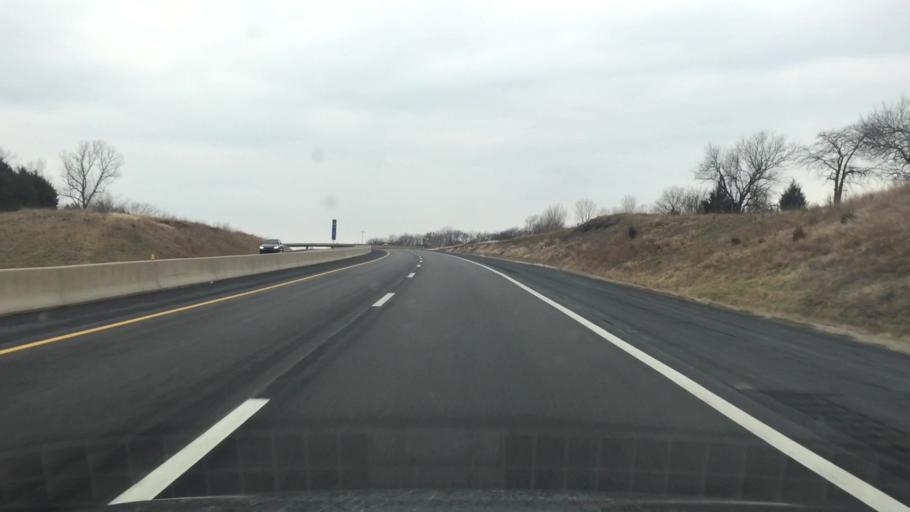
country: US
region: Kansas
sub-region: Shawnee County
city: Auburn
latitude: 38.8907
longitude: -95.8119
